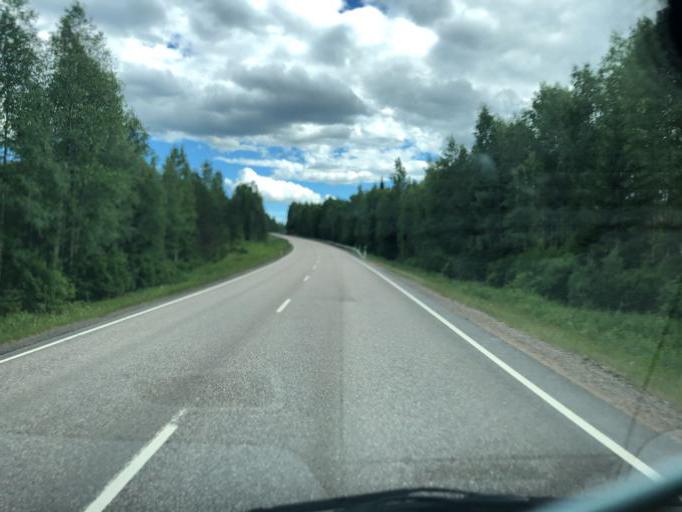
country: FI
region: Southern Savonia
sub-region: Mikkeli
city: Maentyharju
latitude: 61.1151
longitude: 27.0986
